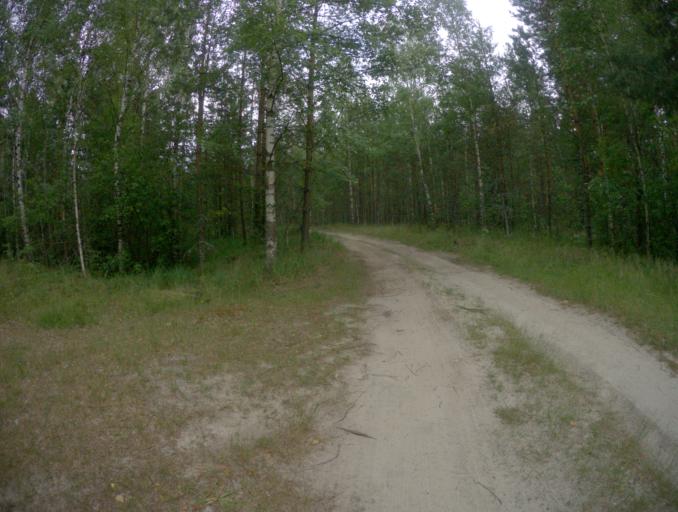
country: RU
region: Nizjnij Novgorod
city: Frolishchi
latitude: 56.4580
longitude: 42.6737
